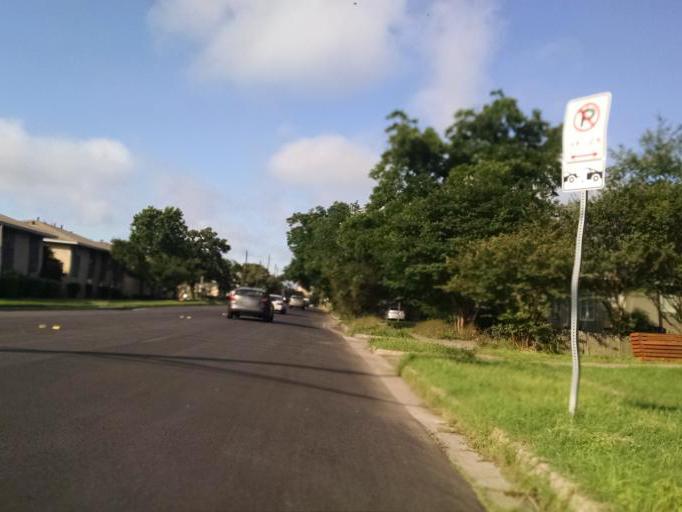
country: US
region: Texas
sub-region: Travis County
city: Austin
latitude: 30.2994
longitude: -97.7344
